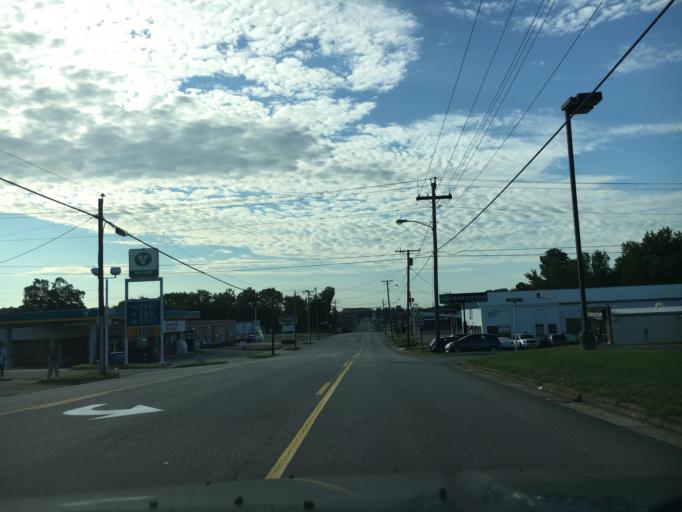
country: US
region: Virginia
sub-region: Halifax County
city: South Boston
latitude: 36.7048
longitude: -78.9090
